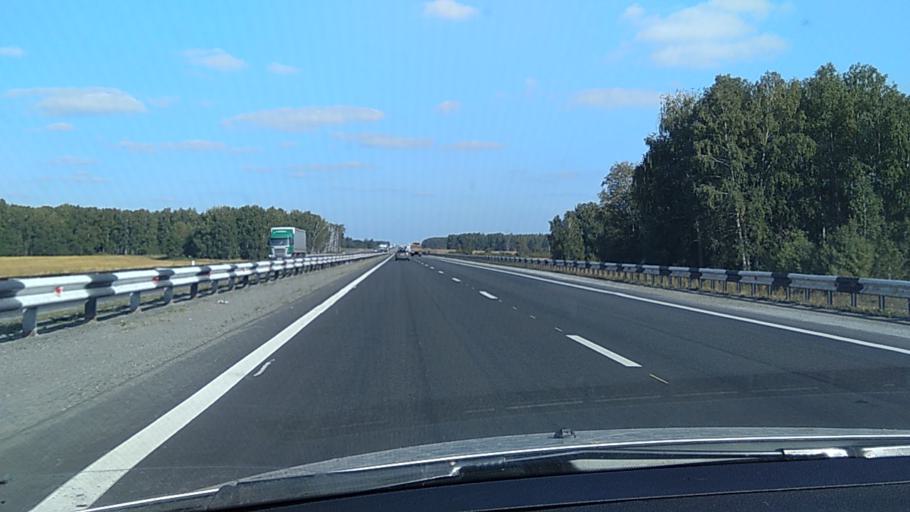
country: RU
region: Chelyabinsk
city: Timiryazevskiy
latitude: 54.9469
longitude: 60.8341
